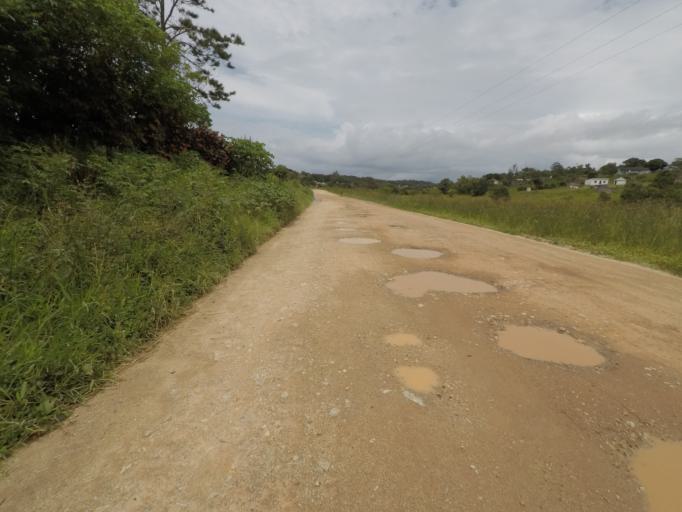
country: ZA
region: KwaZulu-Natal
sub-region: uThungulu District Municipality
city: eSikhawini
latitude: -28.9239
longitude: 31.8330
